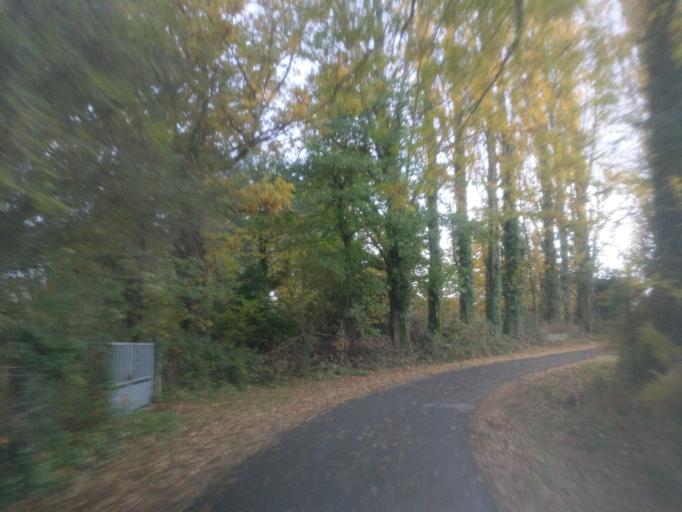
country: FR
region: Brittany
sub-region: Departement d'Ille-et-Vilaine
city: Guichen
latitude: 48.0055
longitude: -1.7831
